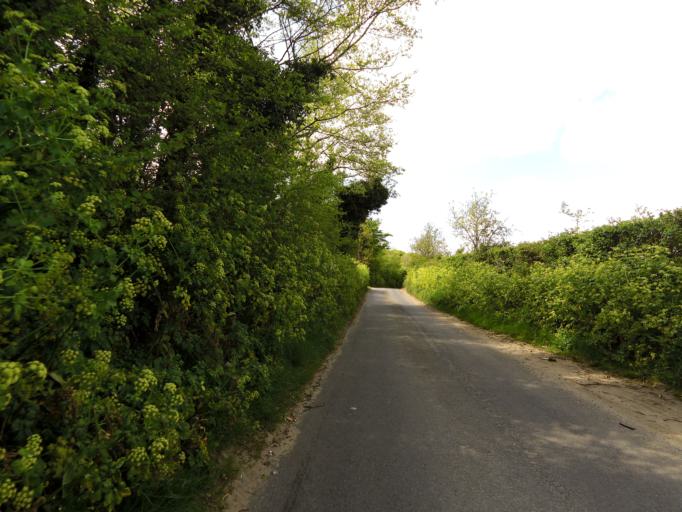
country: GB
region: England
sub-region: Suffolk
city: Kessingland
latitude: 52.4421
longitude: 1.6602
